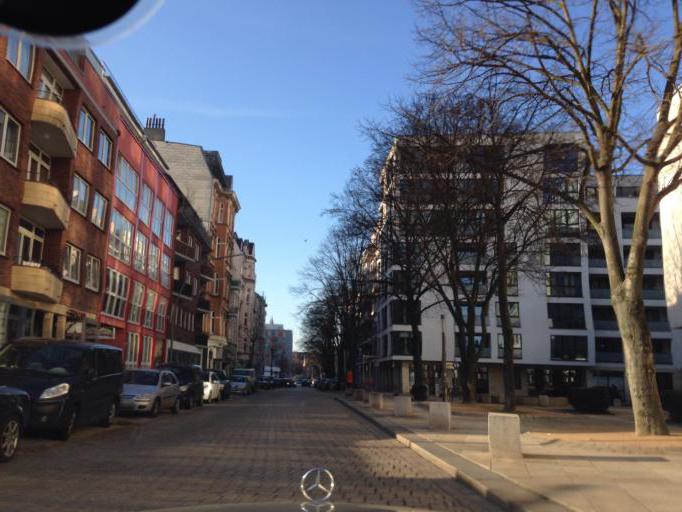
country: DE
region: Hamburg
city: Hamburg-Mitte
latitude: 53.5533
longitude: 10.0191
